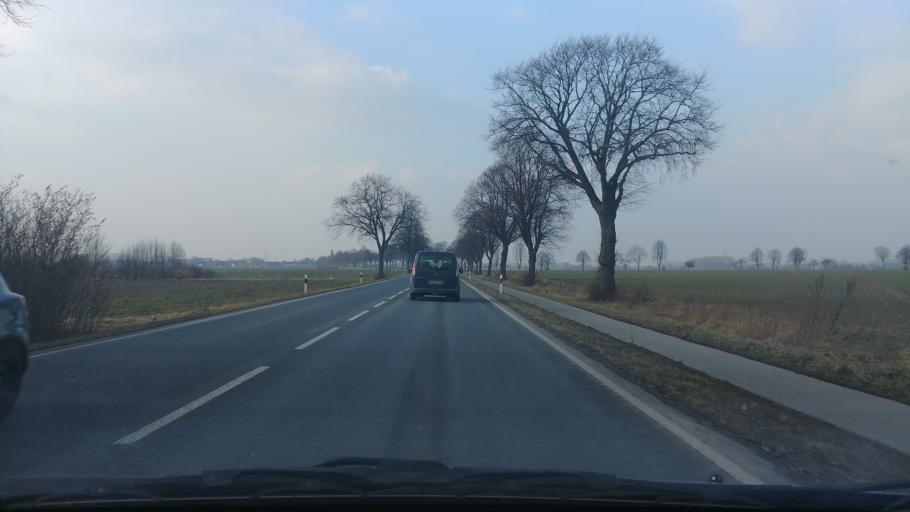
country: DE
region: Lower Saxony
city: Pattensen
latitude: 52.2857
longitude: 9.7560
